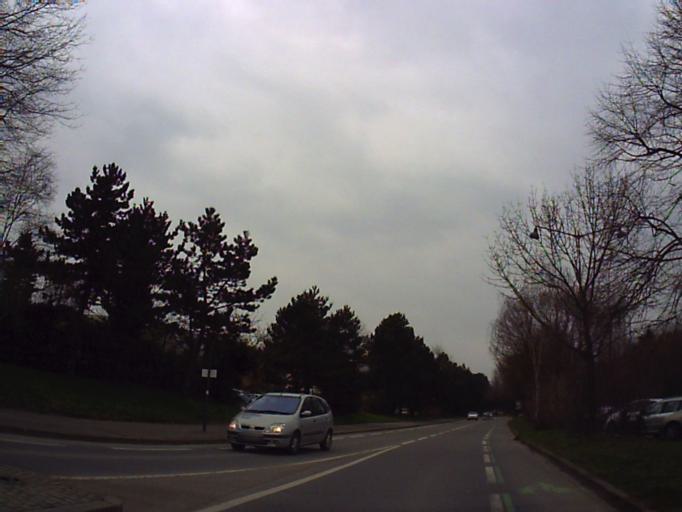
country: FR
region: Brittany
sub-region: Departement d'Ille-et-Vilaine
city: Rennes
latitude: 48.1326
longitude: -1.6520
